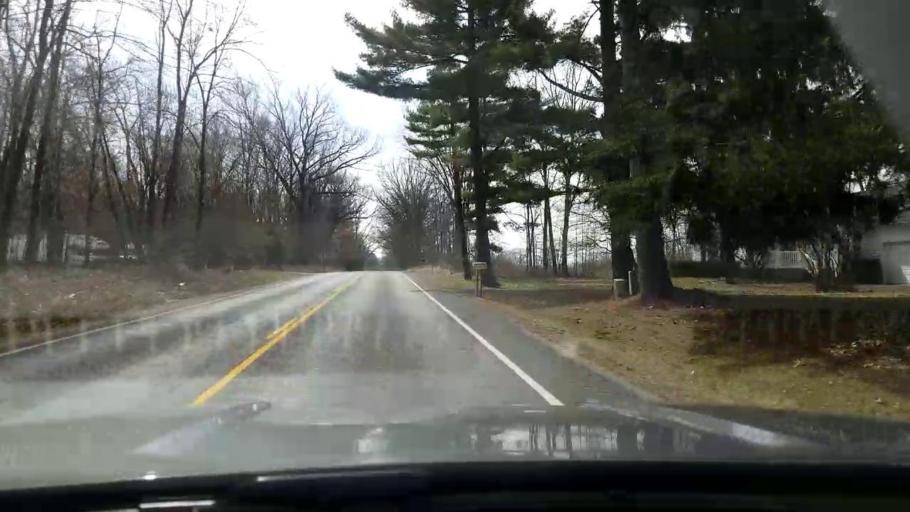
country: US
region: Michigan
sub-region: Jackson County
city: Spring Arbor
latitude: 42.1885
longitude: -84.5206
